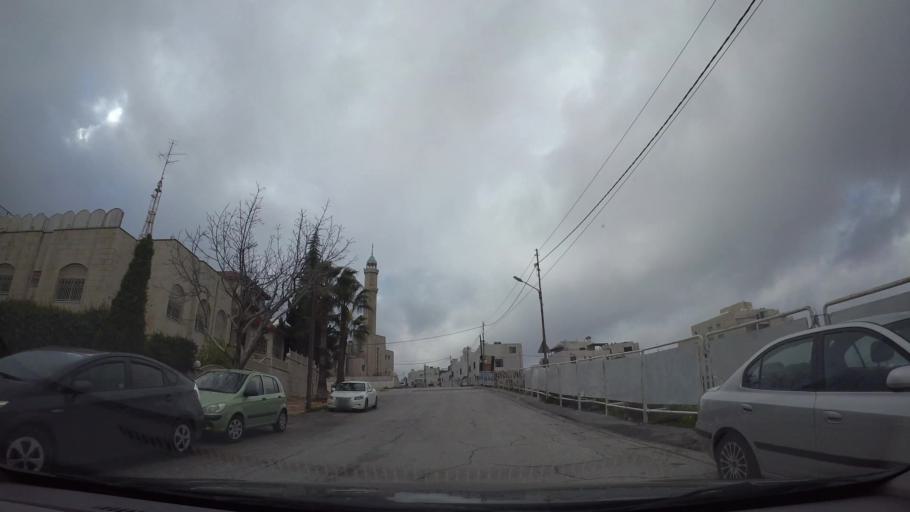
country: JO
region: Amman
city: Amman
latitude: 31.9418
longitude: 35.9045
